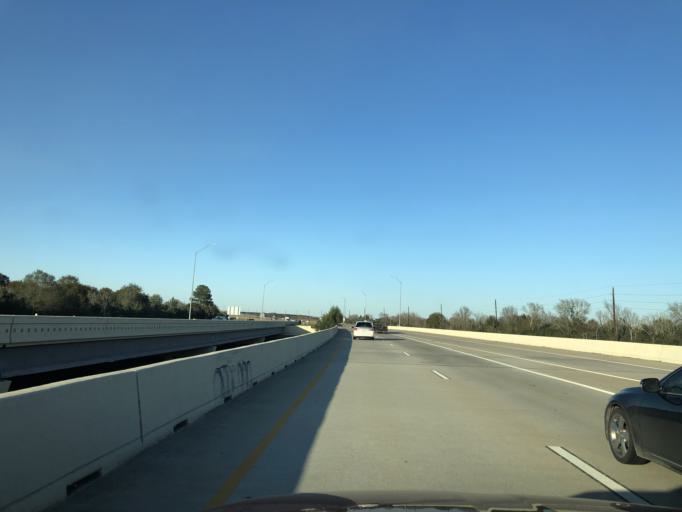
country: US
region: Texas
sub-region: Harris County
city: Katy
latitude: 29.8352
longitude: -95.7580
